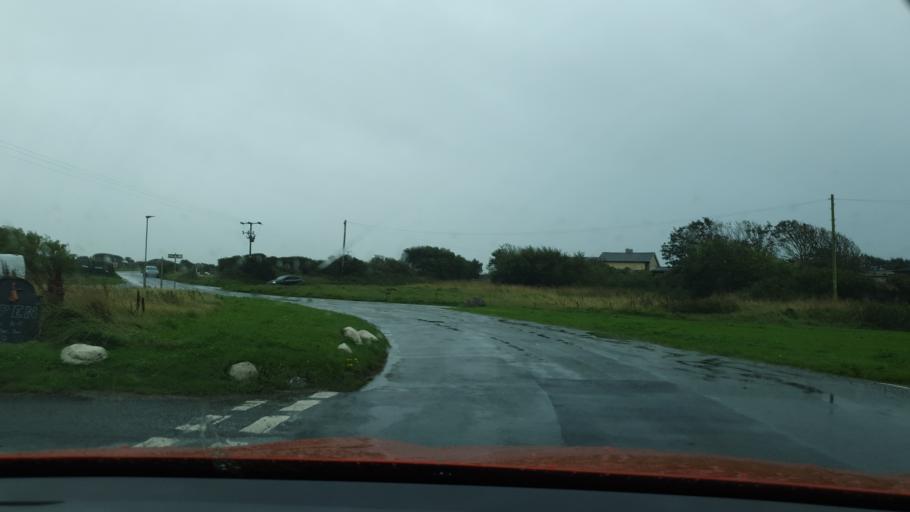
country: GB
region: England
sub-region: Cumbria
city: Barrow in Furness
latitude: 54.0845
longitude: -3.2382
